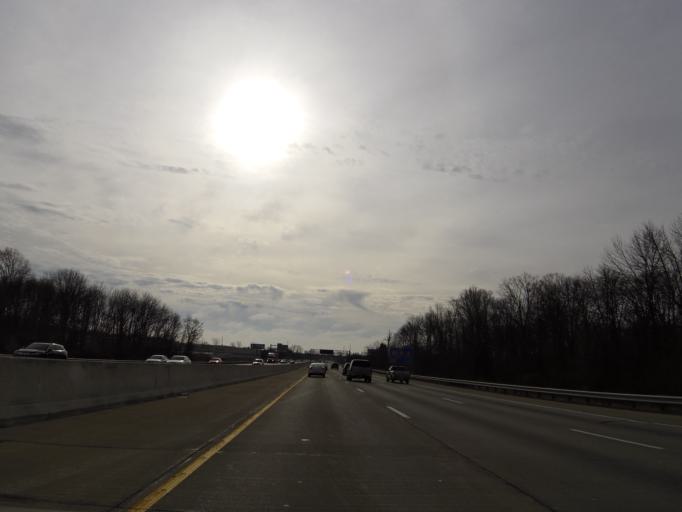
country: US
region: Indiana
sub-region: Marion County
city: Warren Park
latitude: 39.7668
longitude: -86.0294
